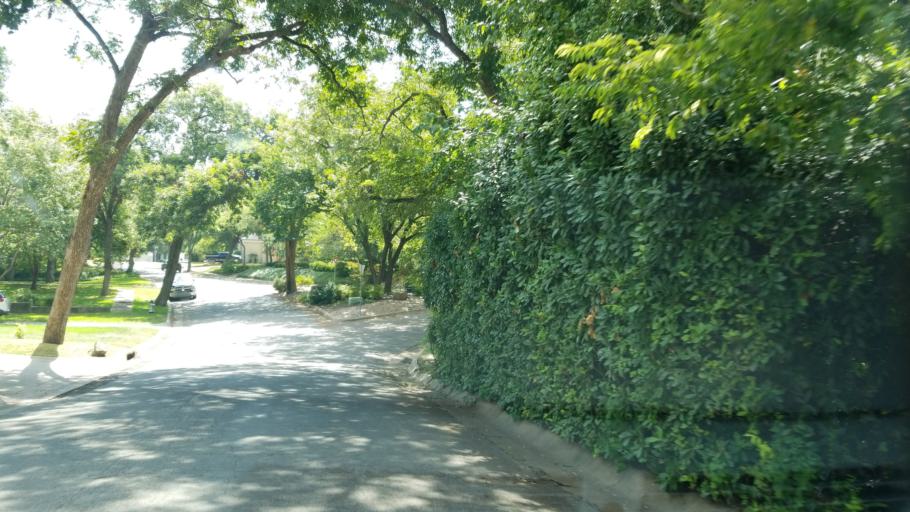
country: US
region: Texas
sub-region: Dallas County
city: Cockrell Hill
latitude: 32.7564
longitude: -96.8453
